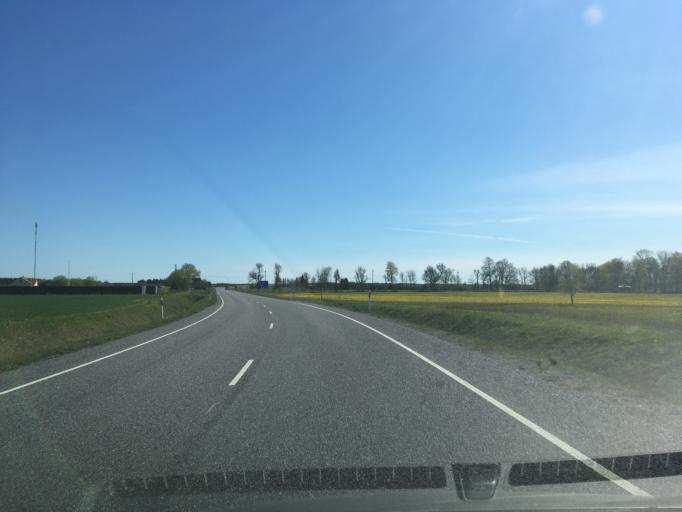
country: EE
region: Harju
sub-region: Rae vald
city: Vaida
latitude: 59.2588
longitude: 25.0181
